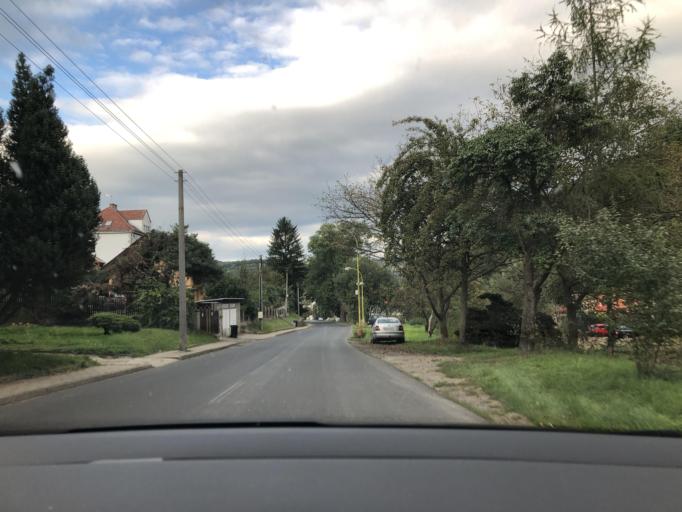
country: CZ
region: Ustecky
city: Velke Brezno
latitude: 50.6567
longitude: 14.1396
